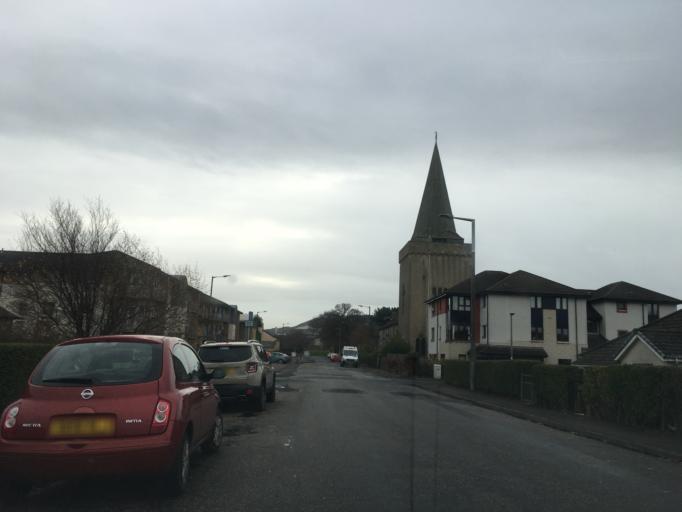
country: GB
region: Scotland
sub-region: Edinburgh
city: Colinton
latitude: 55.9320
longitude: -3.2653
